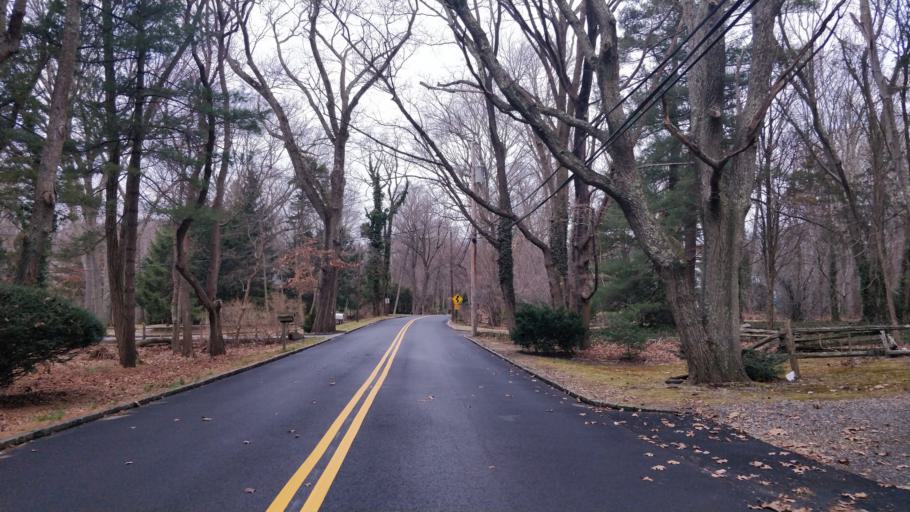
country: US
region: New York
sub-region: Nassau County
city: Laurel Hollow
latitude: 40.8558
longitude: -73.4808
